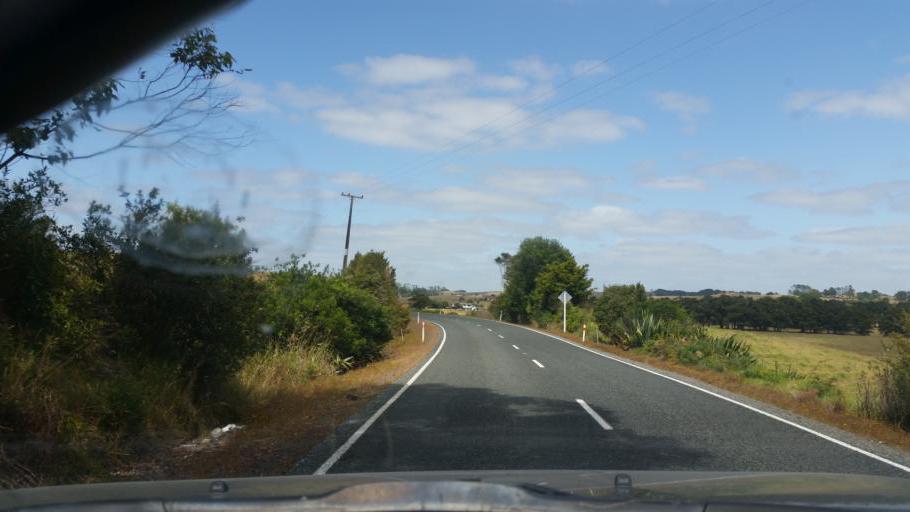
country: NZ
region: Northland
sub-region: Whangarei
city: Ruakaka
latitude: -35.9601
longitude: 174.2916
